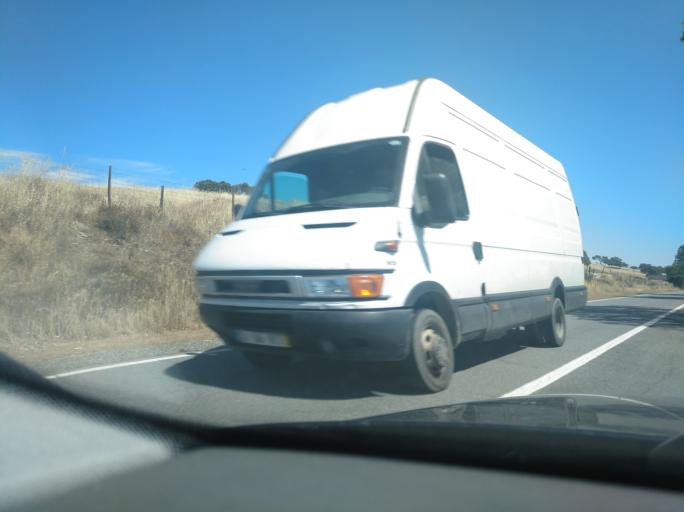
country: PT
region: Beja
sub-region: Castro Verde
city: Castro Verde
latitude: 37.6792
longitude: -8.0833
